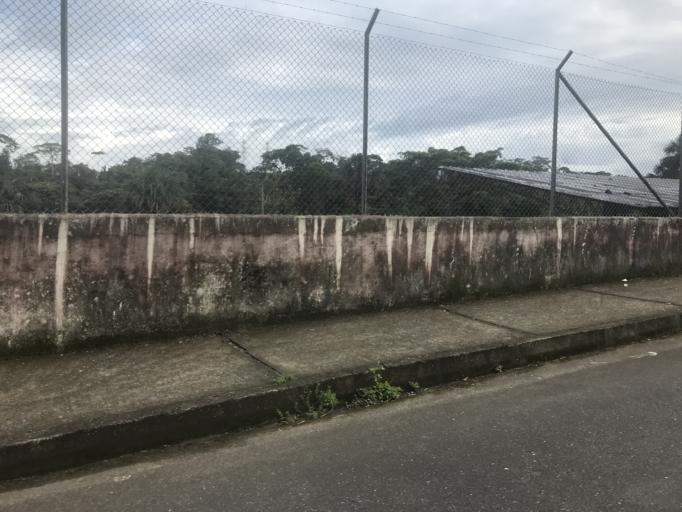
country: EC
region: Napo
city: Tena
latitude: -1.0428
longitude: -77.7973
